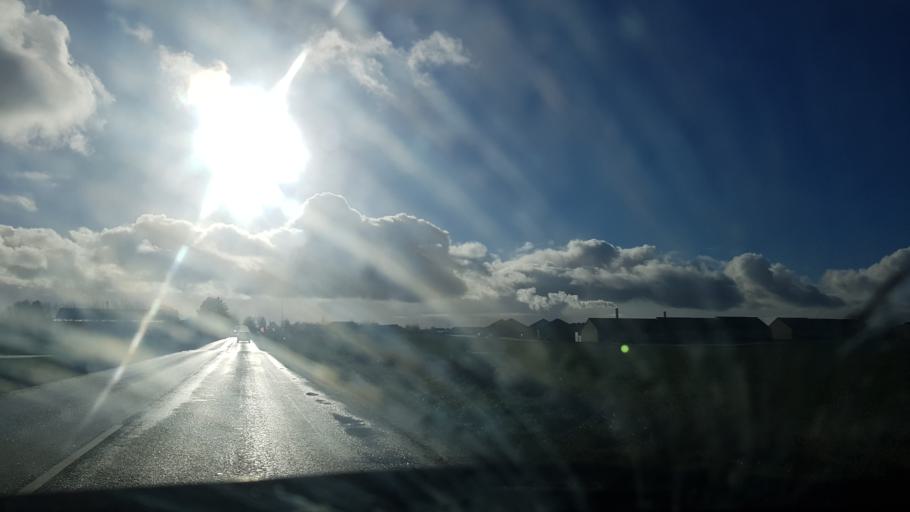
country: DK
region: South Denmark
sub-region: Fredericia Kommune
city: Taulov
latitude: 55.5226
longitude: 9.6369
